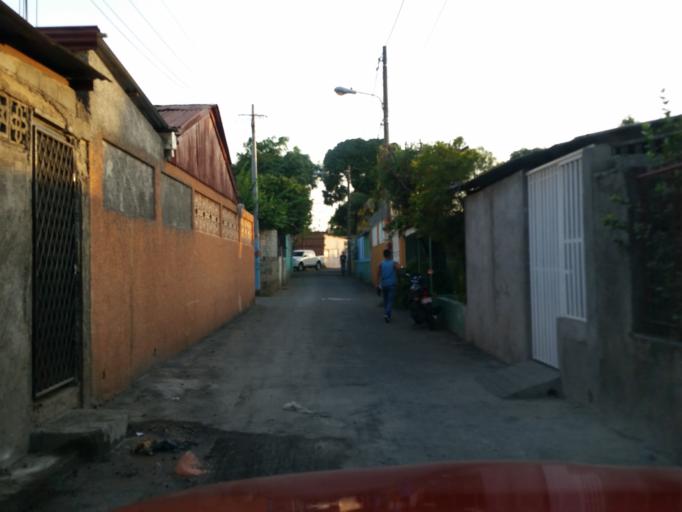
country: NI
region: Managua
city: Managua
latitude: 12.1377
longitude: -86.2579
